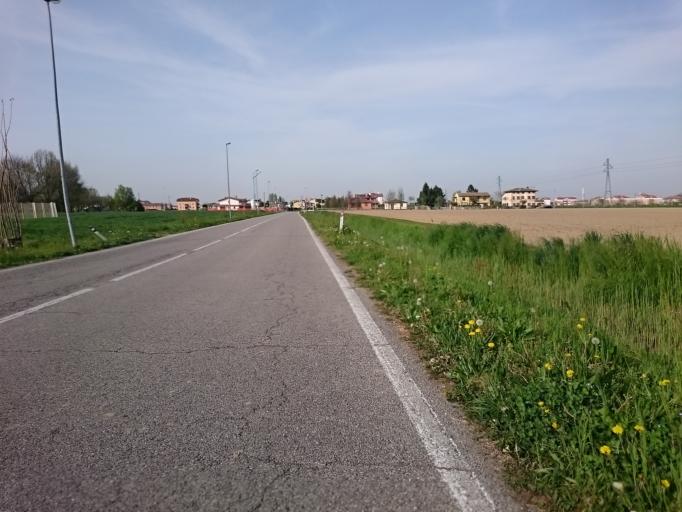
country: IT
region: Veneto
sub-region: Provincia di Padova
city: Masera di Padova
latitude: 45.3331
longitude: 11.8690
